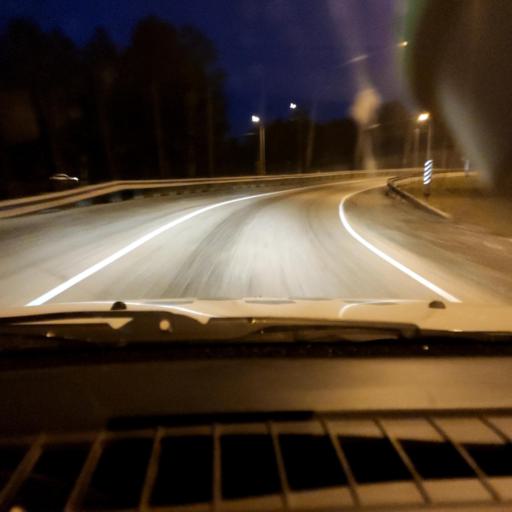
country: RU
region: Sverdlovsk
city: Talitsa
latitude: 56.8501
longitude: 60.0595
